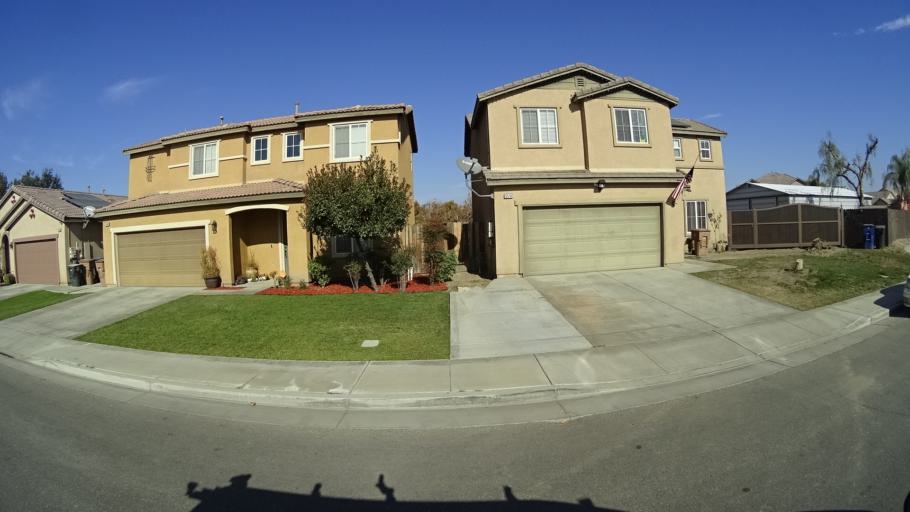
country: US
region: California
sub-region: Kern County
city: Greenfield
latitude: 35.2771
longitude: -119.0644
